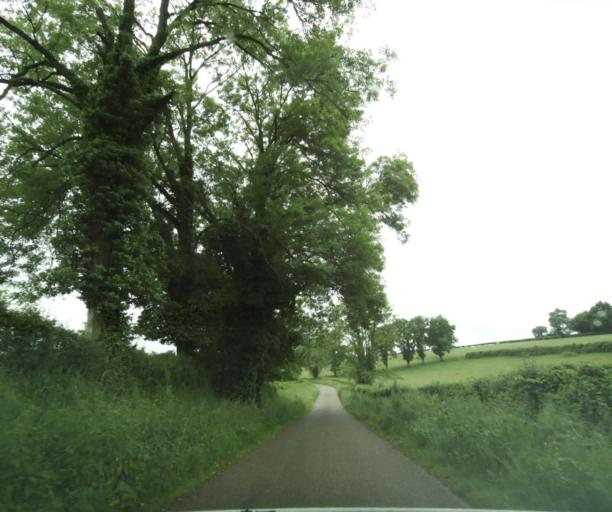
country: FR
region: Bourgogne
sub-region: Departement de Saone-et-Loire
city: Charolles
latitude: 46.4367
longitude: 4.3440
